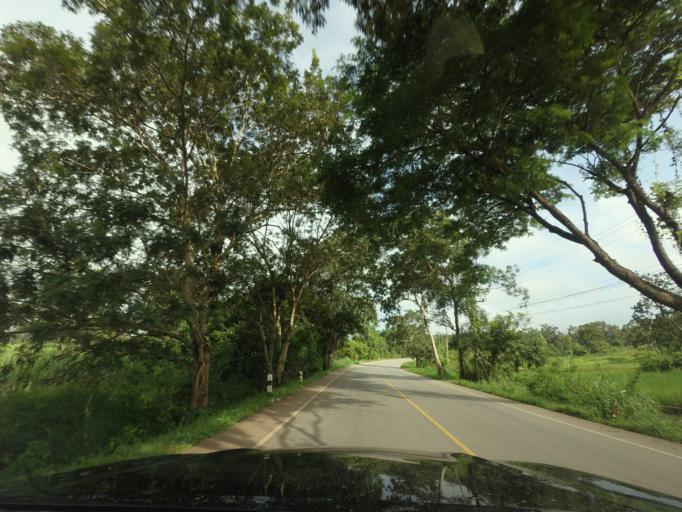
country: TH
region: Changwat Udon Thani
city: Nam Som
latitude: 17.8421
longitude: 102.2560
